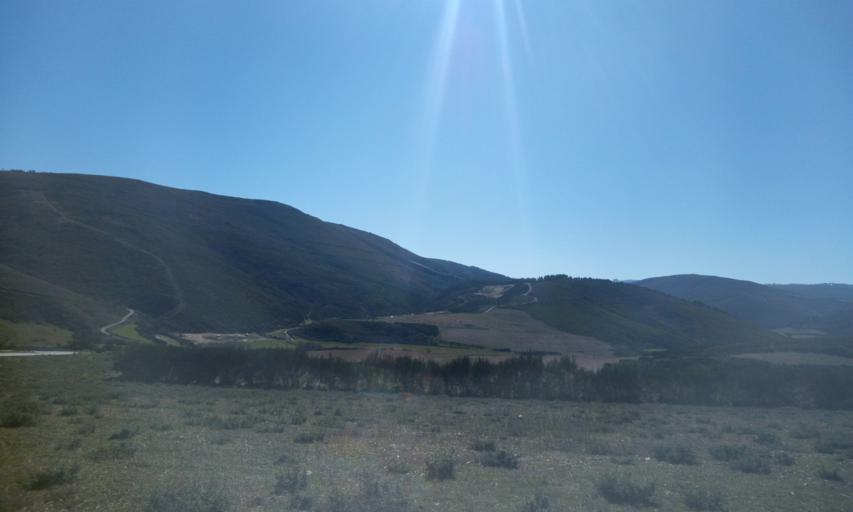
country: PT
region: Guarda
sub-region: Manteigas
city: Manteigas
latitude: 40.4595
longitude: -7.4953
